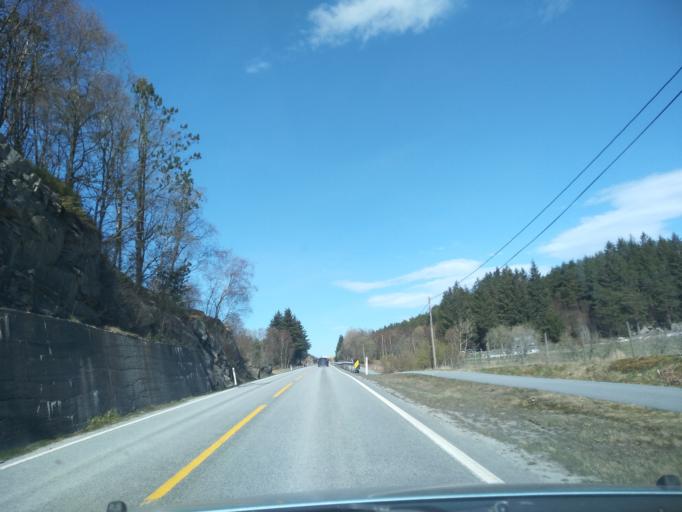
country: NO
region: Rogaland
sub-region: Tysvaer
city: Tysvaer
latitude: 59.3247
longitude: 5.4460
